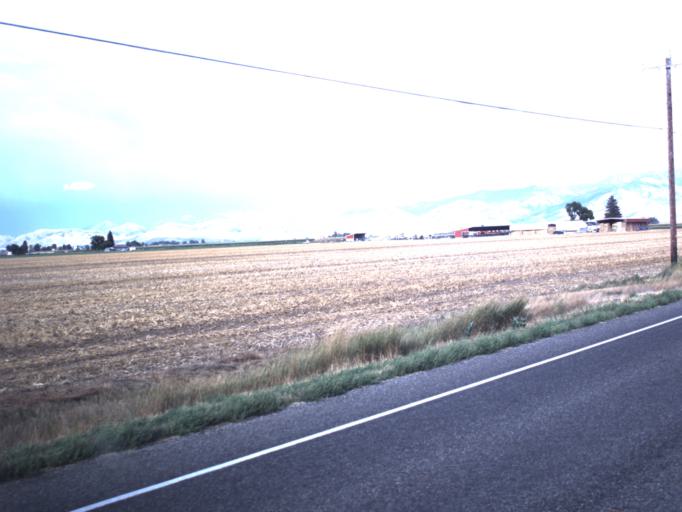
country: US
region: Utah
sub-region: Cache County
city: Lewiston
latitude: 41.9754
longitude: -111.9223
